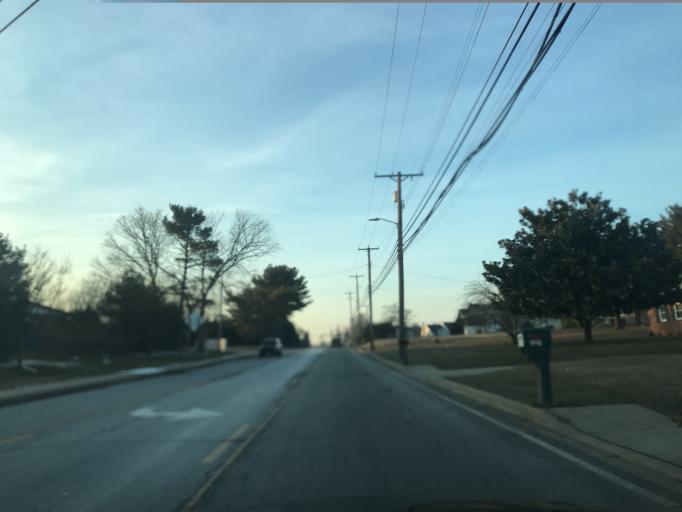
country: US
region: Maryland
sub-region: Harford County
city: Edgewood
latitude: 39.4276
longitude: -76.3002
